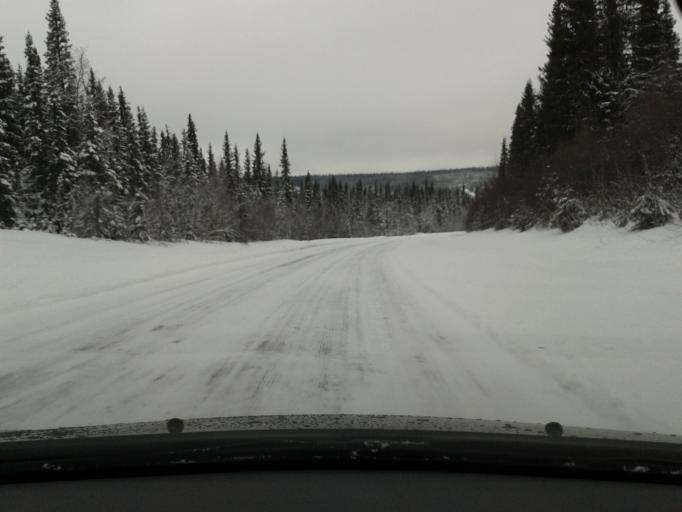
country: SE
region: Vaesterbotten
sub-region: Vilhelmina Kommun
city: Sjoberg
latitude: 65.0349
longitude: 15.9013
